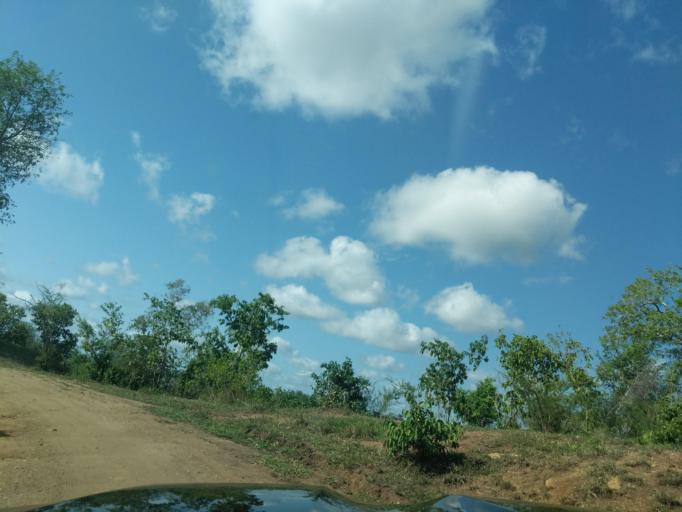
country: TZ
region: Tanga
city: Muheza
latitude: -5.4231
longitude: 38.6476
